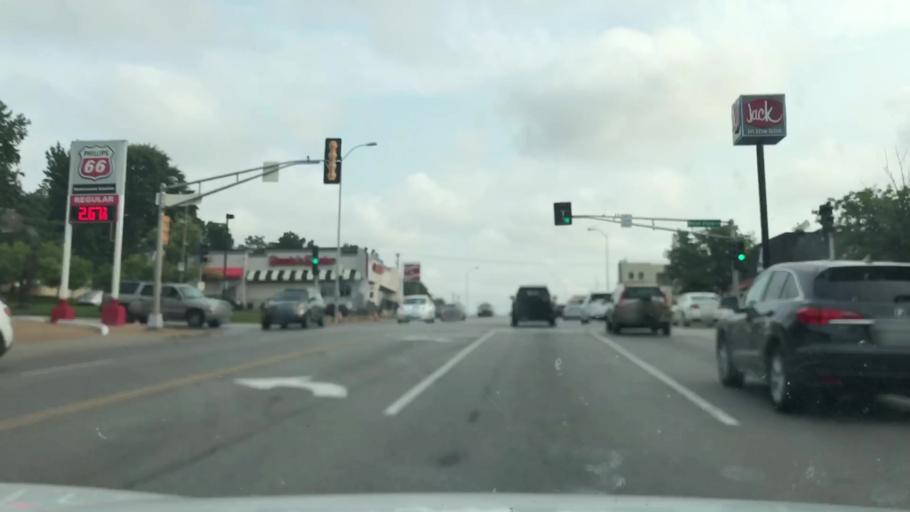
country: US
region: Missouri
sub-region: Saint Louis County
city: Richmond Heights
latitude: 38.6263
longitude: -90.2876
